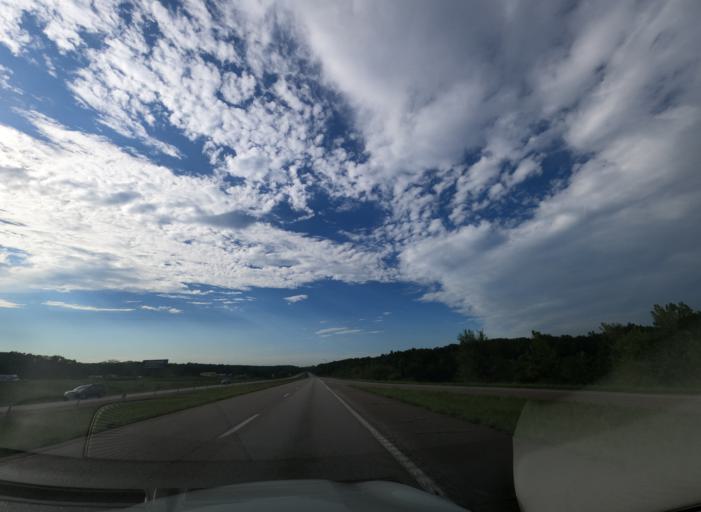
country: US
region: Missouri
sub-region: Jefferson County
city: Crystal City
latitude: 38.0555
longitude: -90.2757
